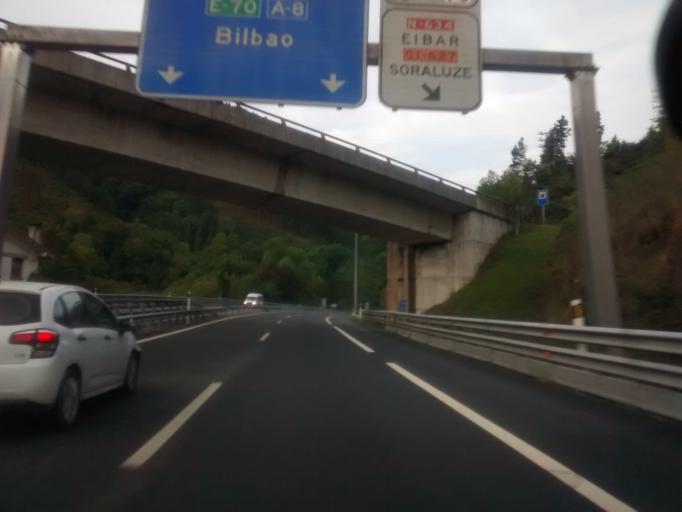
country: ES
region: Basque Country
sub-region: Provincia de Guipuzcoa
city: Elgoibar
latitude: 43.1943
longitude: -2.4380
